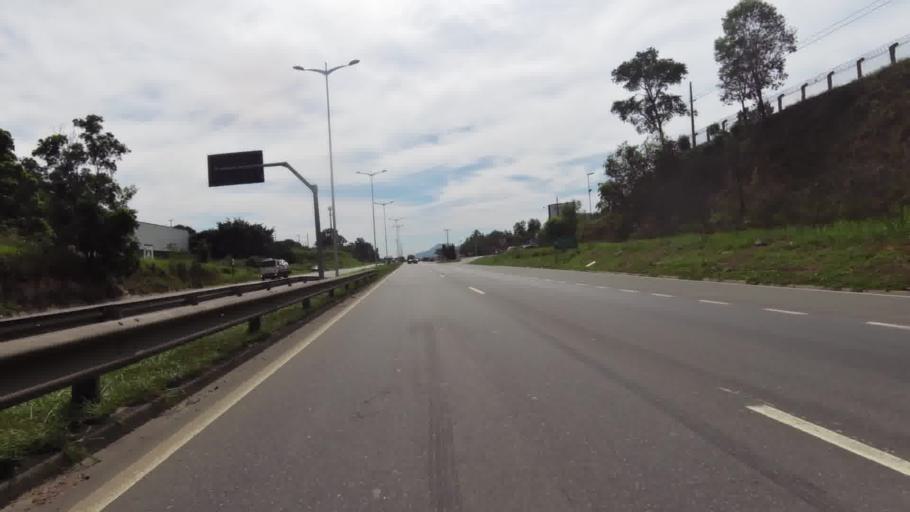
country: BR
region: Espirito Santo
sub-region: Vitoria
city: Vitoria
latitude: -20.2969
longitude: -40.3942
